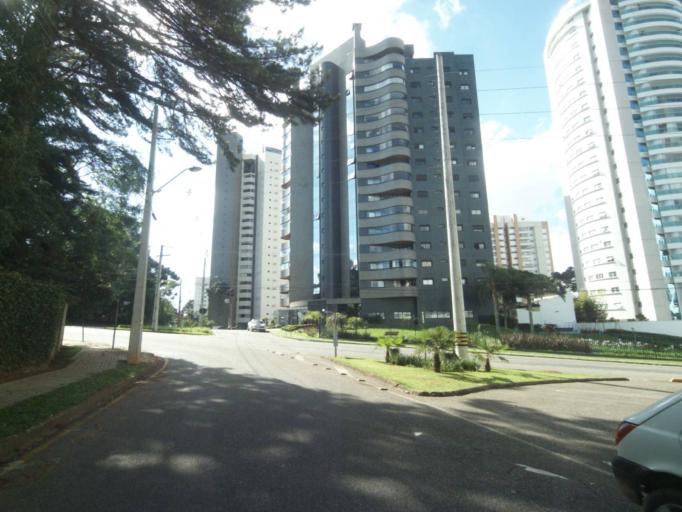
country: BR
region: Parana
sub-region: Curitiba
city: Curitiba
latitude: -25.4389
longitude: -49.3307
